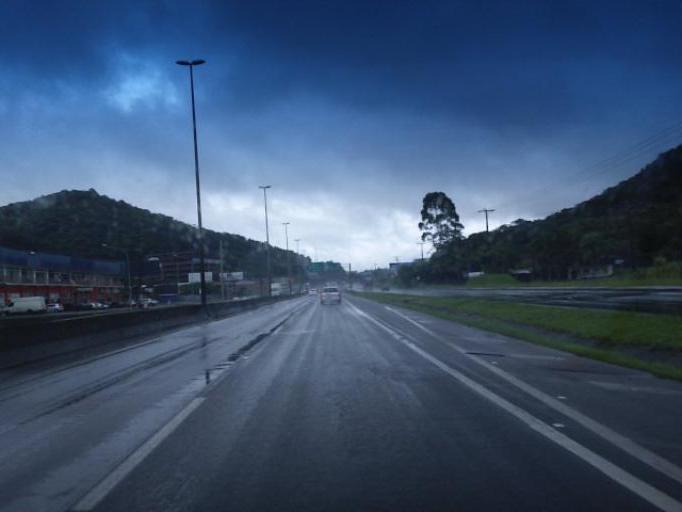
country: BR
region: Santa Catarina
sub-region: Balneario Camboriu
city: Balneario Camboriu
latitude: -26.9950
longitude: -48.6582
